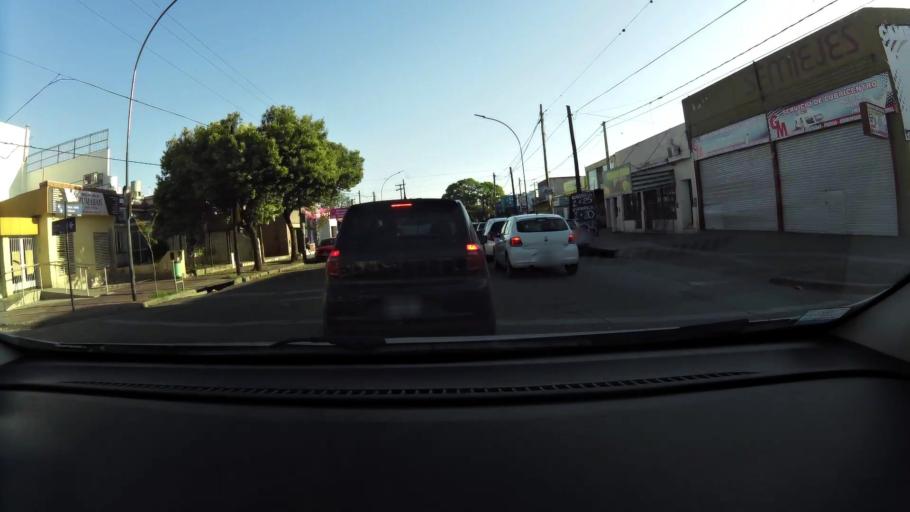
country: AR
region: Cordoba
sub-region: Departamento de Capital
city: Cordoba
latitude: -31.3752
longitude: -64.2065
